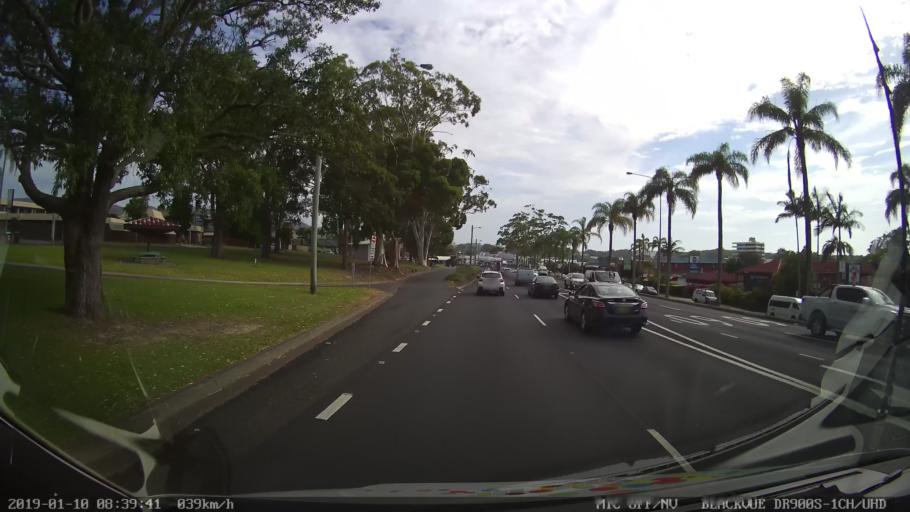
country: AU
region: New South Wales
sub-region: Coffs Harbour
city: Coffs Harbour
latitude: -30.3005
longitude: 153.1107
